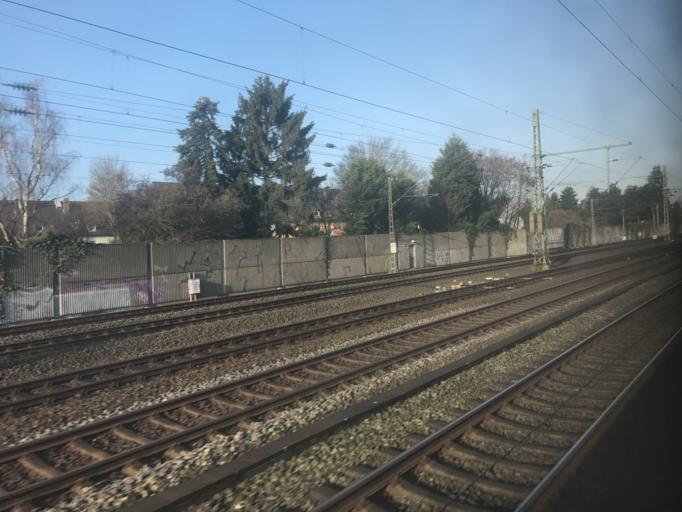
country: DE
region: North Rhine-Westphalia
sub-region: Regierungsbezirk Dusseldorf
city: Dusseldorf
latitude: 51.2677
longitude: 6.7899
